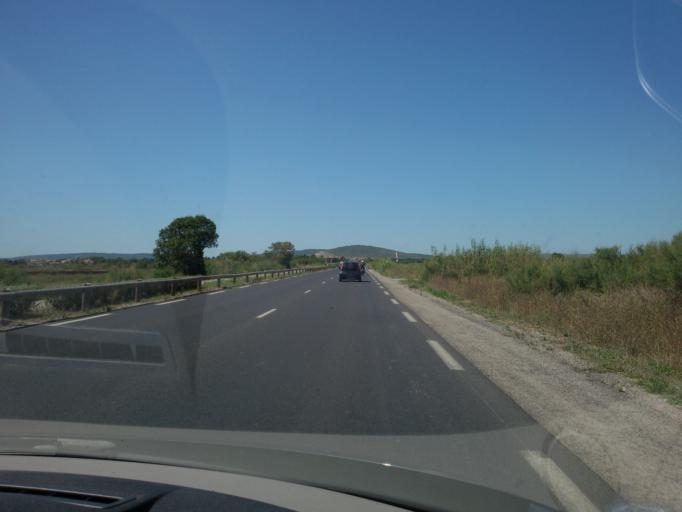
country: FR
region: Languedoc-Roussillon
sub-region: Departement de l'Herault
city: Villeneuve-les-Maguelone
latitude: 43.5394
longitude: 3.8843
